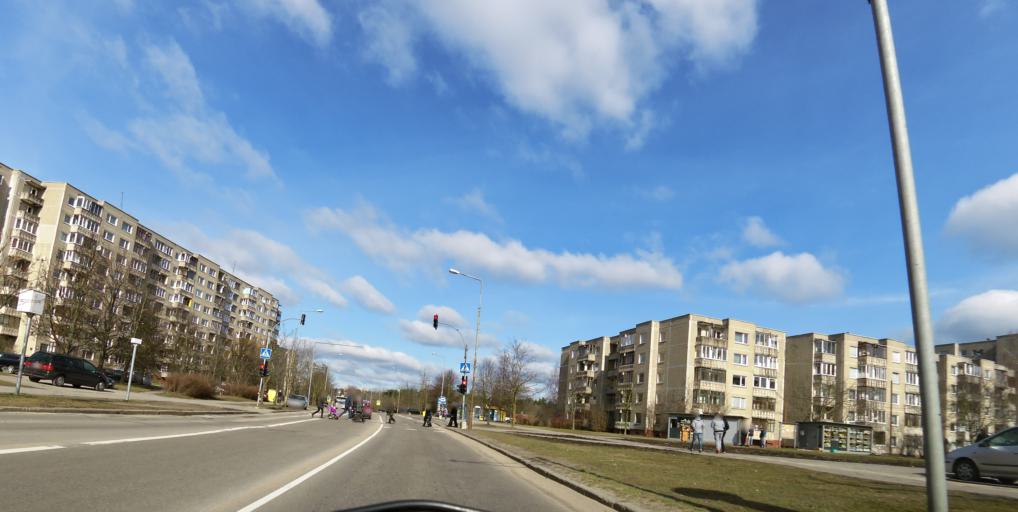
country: LT
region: Vilnius County
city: Seskine
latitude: 54.7178
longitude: 25.2579
